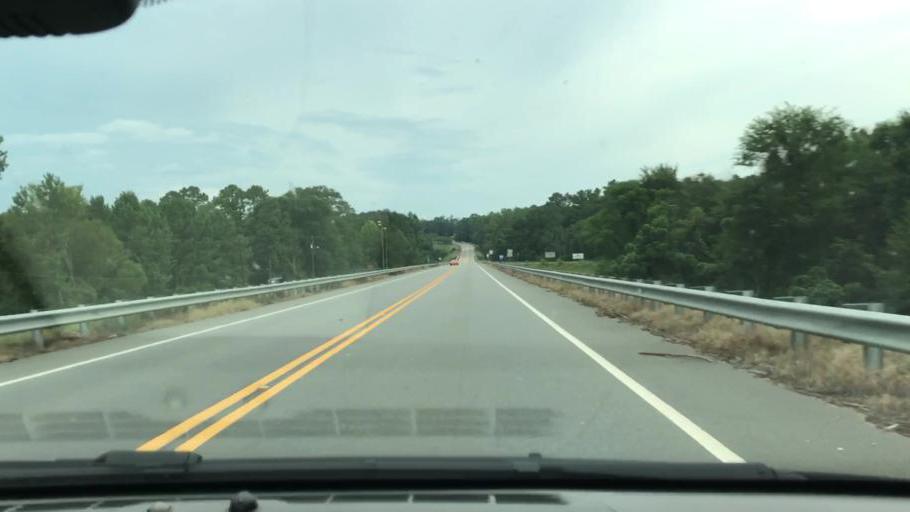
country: US
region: Alabama
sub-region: Houston County
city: Ashford
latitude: 31.2861
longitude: -85.1012
